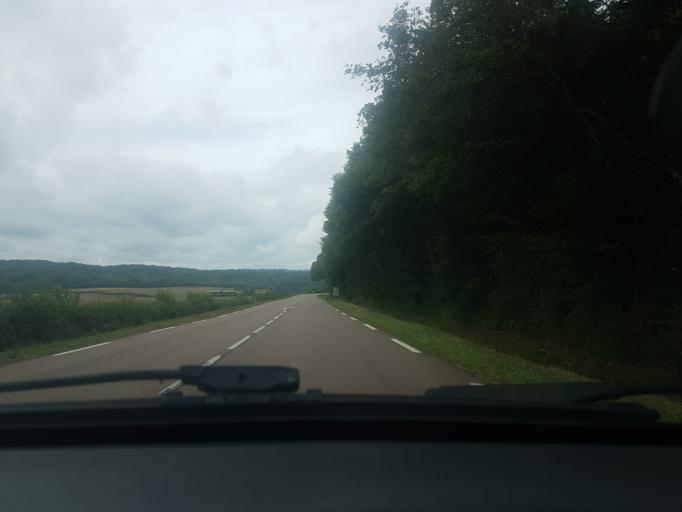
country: FR
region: Bourgogne
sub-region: Departement de la Cote-d'Or
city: Saulieu
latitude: 47.2435
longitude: 4.2934
